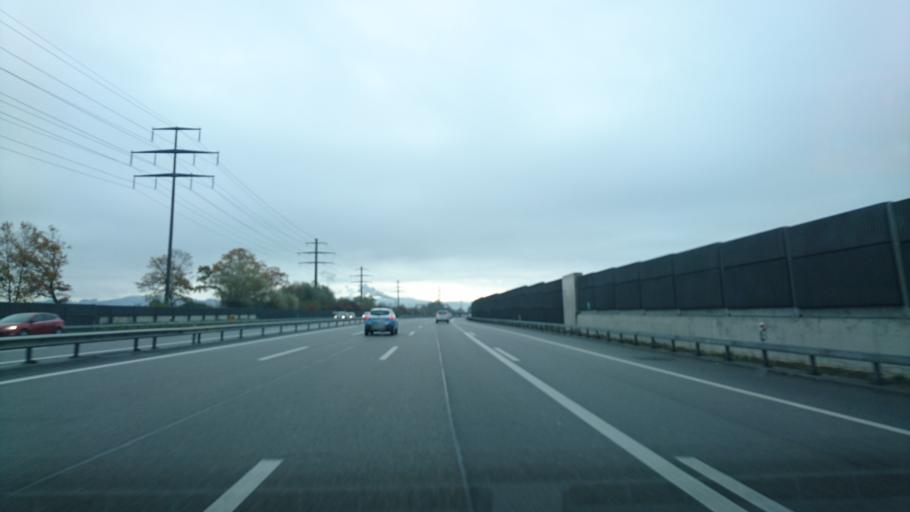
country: CH
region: Aargau
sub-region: Bezirk Zofingen
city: Aarburg
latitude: 47.3104
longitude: 7.9014
